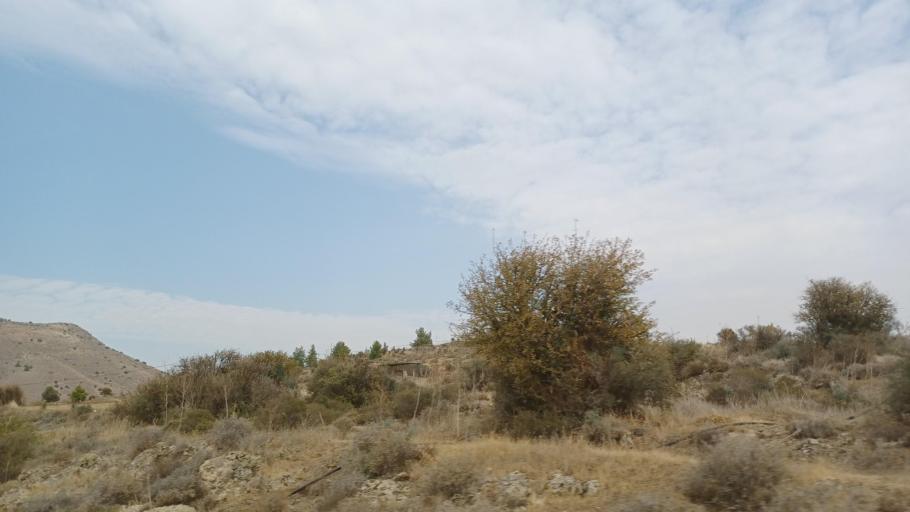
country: CY
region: Lefkosia
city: Klirou
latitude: 35.0350
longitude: 33.1352
